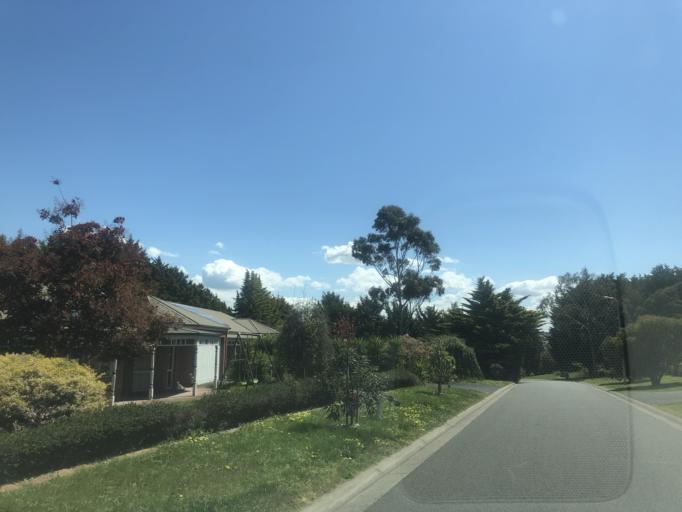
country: AU
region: Victoria
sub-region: Casey
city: Hallam
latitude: -37.9941
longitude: 145.2798
